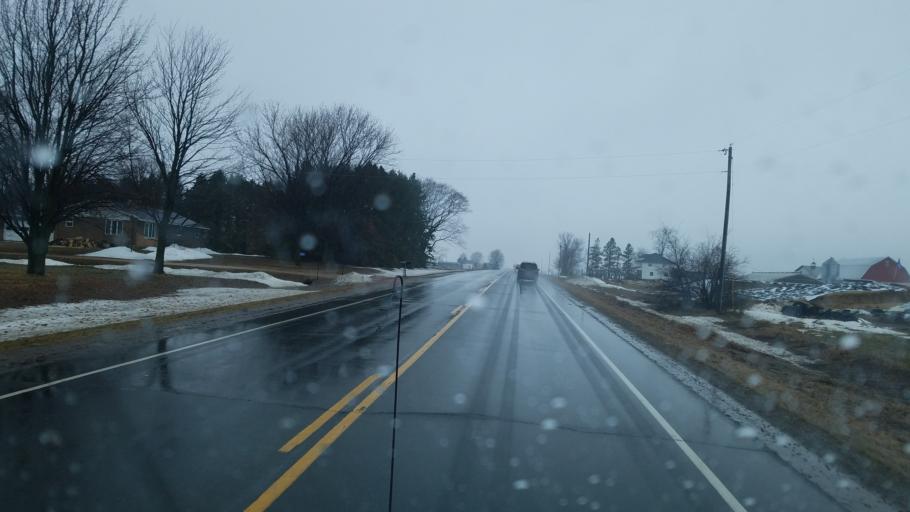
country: US
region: Wisconsin
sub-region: Marathon County
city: Spencer
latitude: 44.6562
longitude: -90.3300
